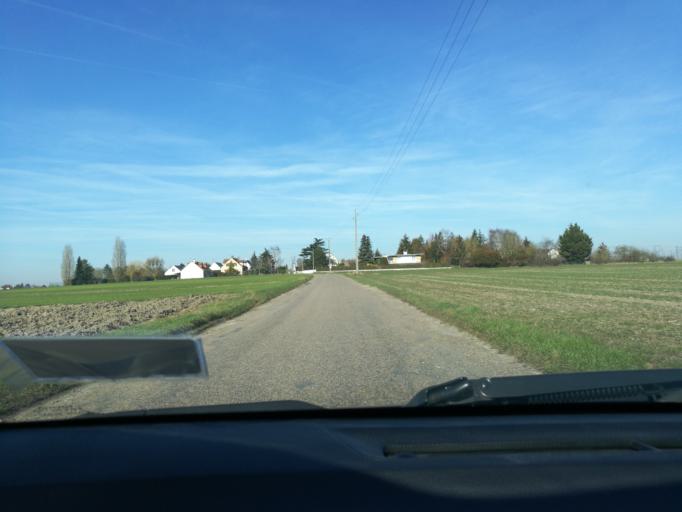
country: FR
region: Centre
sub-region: Departement du Loiret
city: Mareau-aux-Pres
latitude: 47.8828
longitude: 1.7911
